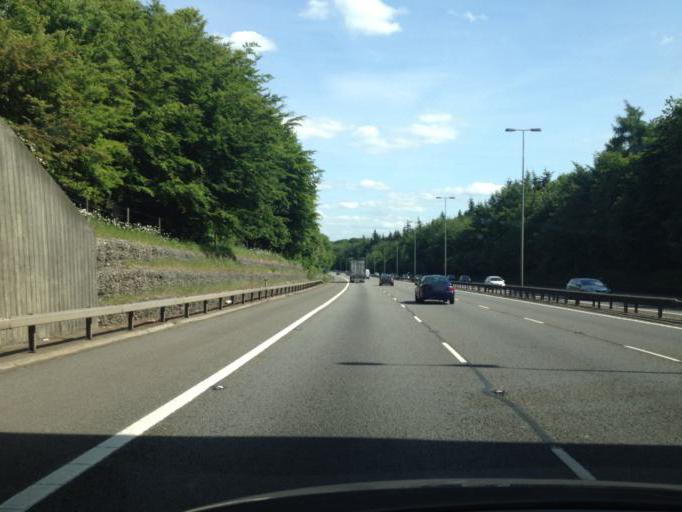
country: GB
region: England
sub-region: Buckinghamshire
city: Stokenchurch
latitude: 51.6353
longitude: -0.8805
